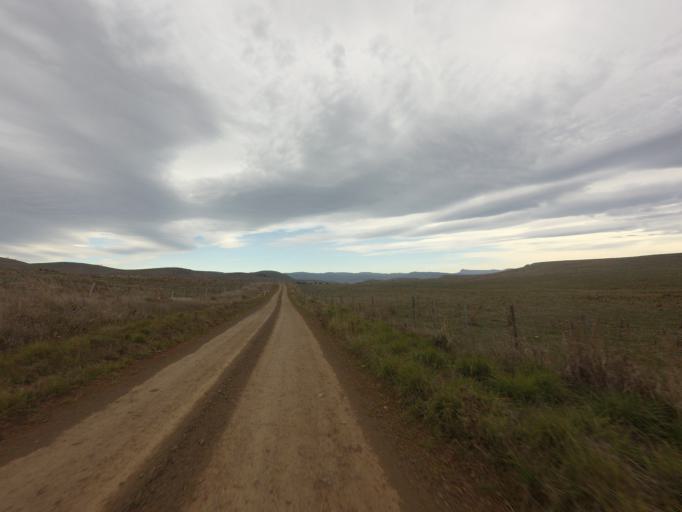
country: AU
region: Tasmania
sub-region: Derwent Valley
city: New Norfolk
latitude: -42.4356
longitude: 146.8076
